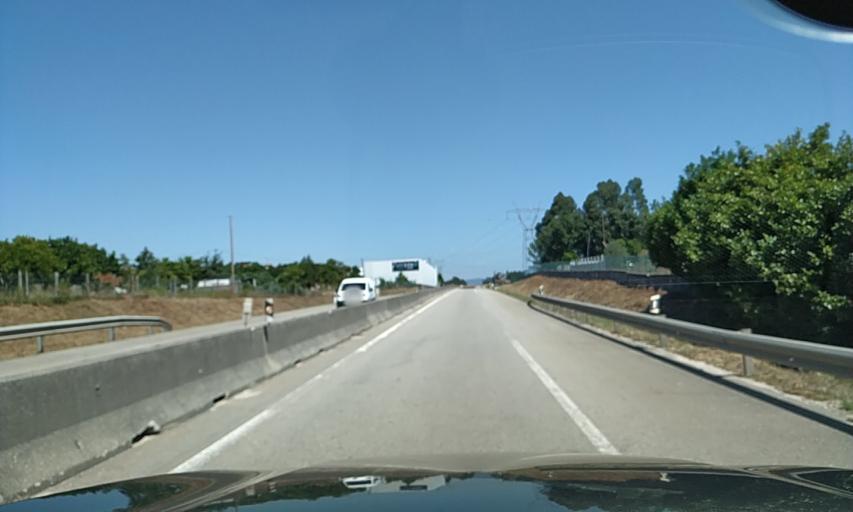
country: PT
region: Aveiro
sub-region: Agueda
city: Agueda
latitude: 40.5758
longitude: -8.4747
